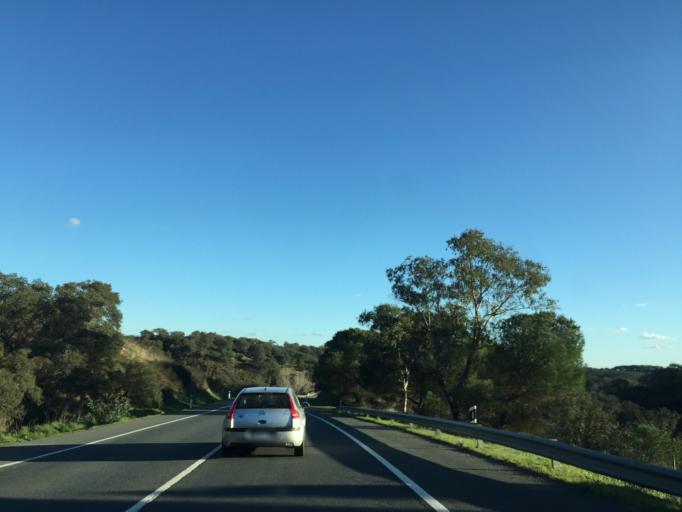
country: PT
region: Setubal
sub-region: Grandola
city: Grandola
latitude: 38.0668
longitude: -8.4128
